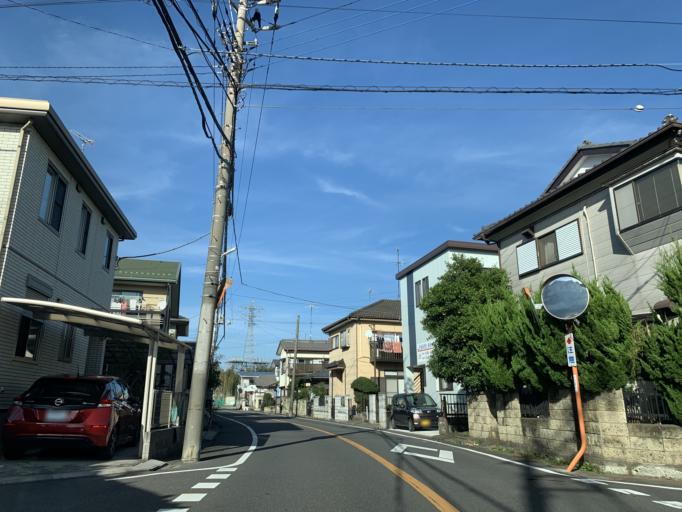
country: JP
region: Chiba
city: Nagareyama
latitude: 35.8968
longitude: 139.9289
